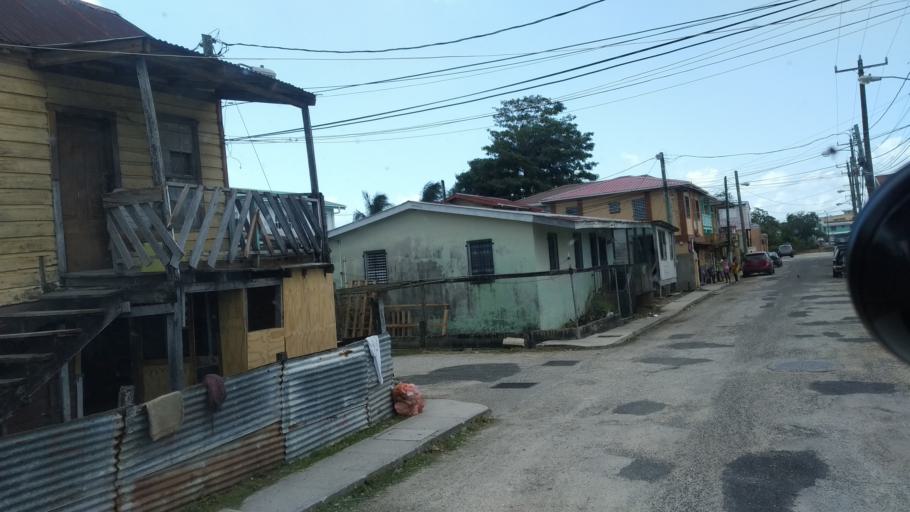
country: BZ
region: Belize
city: Belize City
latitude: 17.4991
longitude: -88.1893
